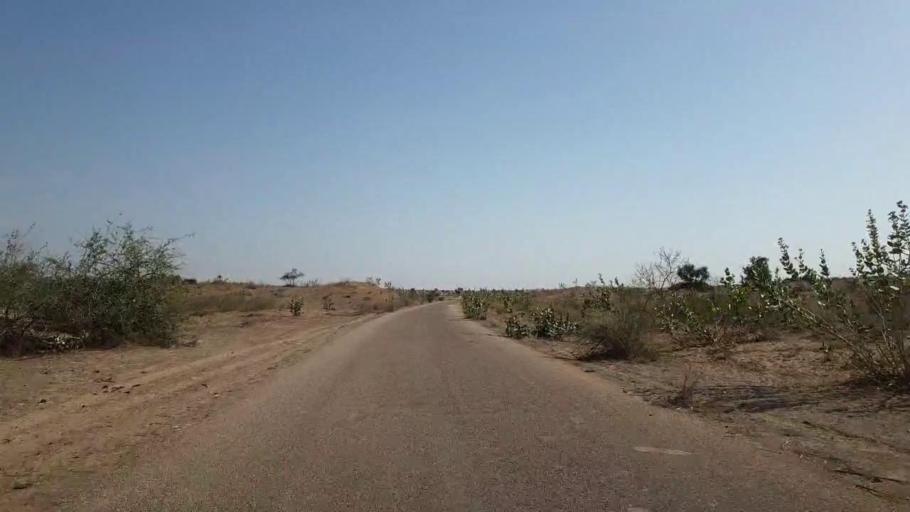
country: PK
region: Sindh
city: Islamkot
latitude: 25.0764
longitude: 70.0433
